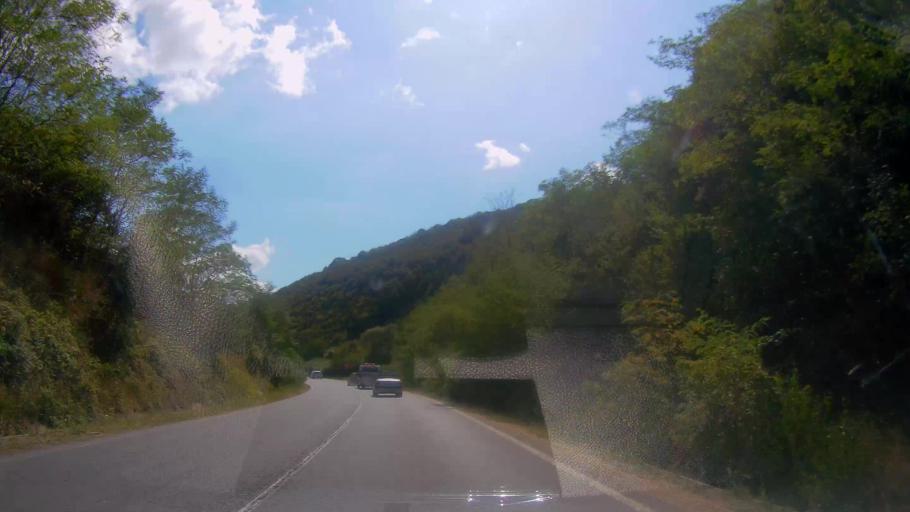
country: BG
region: Stara Zagora
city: Gurkovo
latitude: 42.7369
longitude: 25.7078
